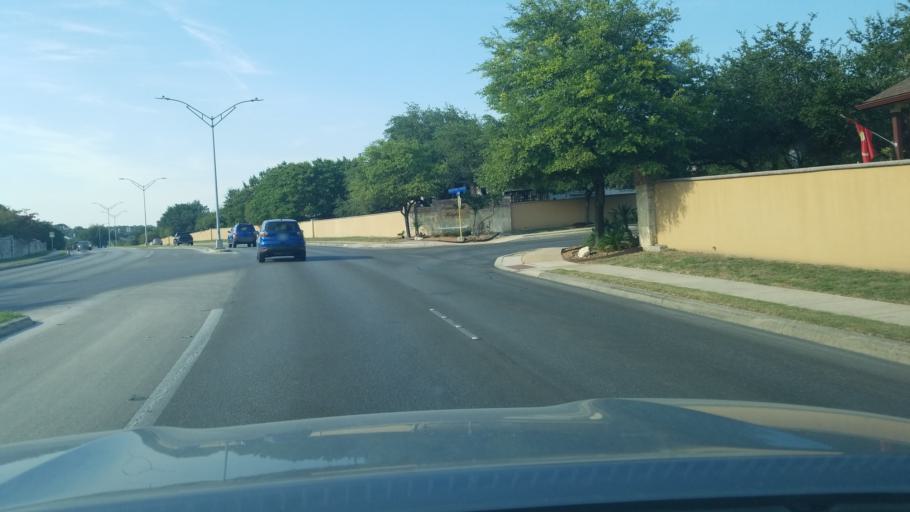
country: US
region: Texas
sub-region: Bexar County
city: Hollywood Park
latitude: 29.6490
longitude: -98.5034
